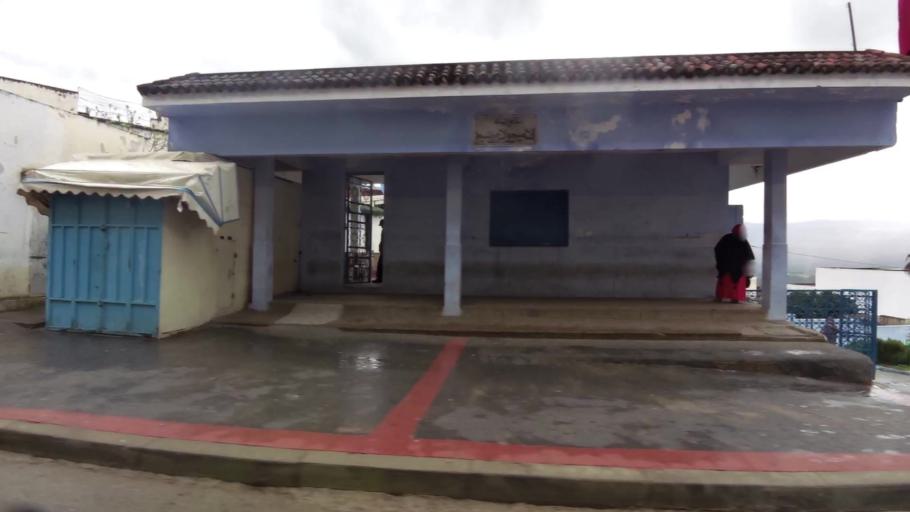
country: MA
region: Tanger-Tetouan
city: Chefchaouene
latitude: 35.1674
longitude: -5.2707
